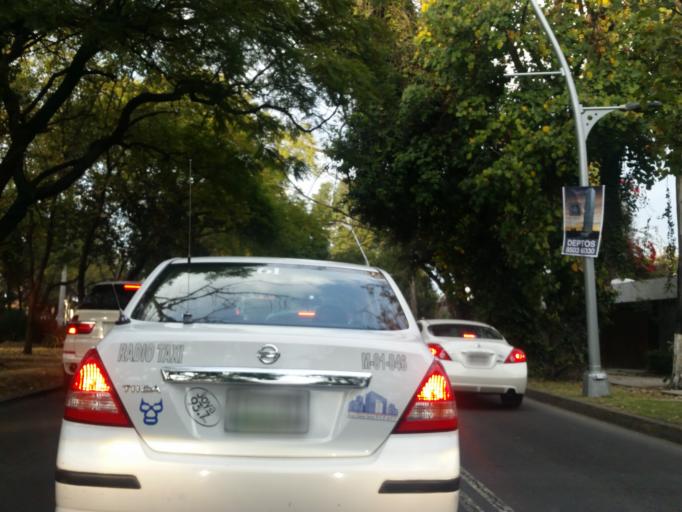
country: MX
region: Mexico City
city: Polanco
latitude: 19.4011
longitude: -99.2325
